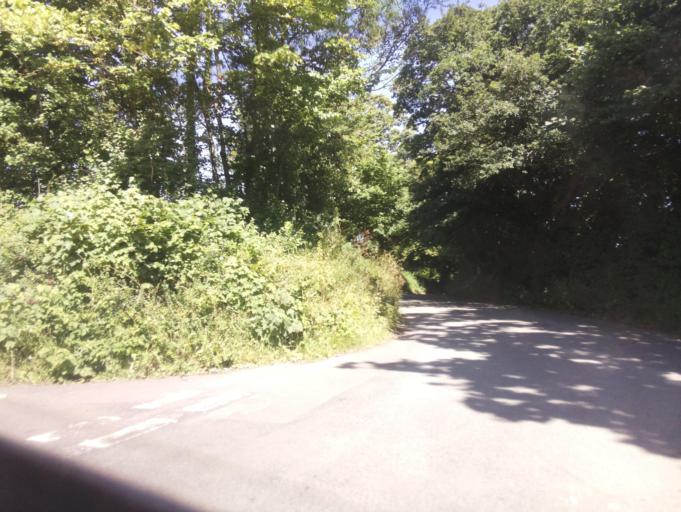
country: GB
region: England
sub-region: Devon
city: Kingskerswell
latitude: 50.4981
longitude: -3.6103
